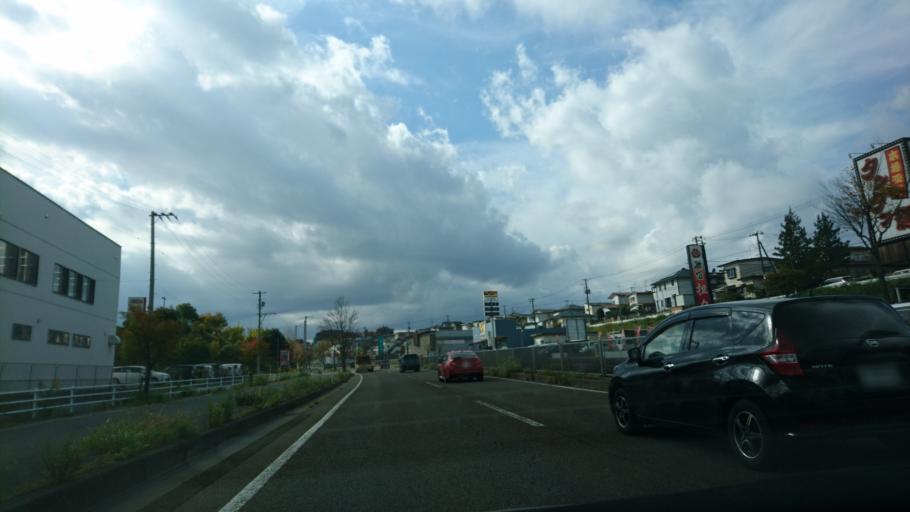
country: JP
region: Miyagi
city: Tomiya
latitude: 38.3672
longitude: 140.8736
